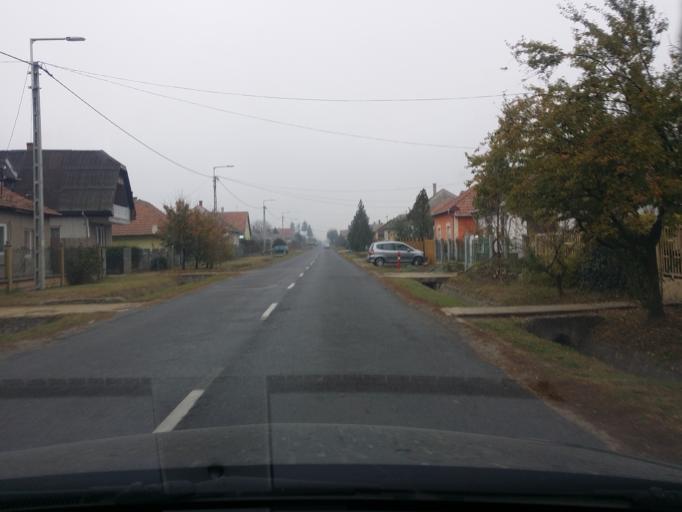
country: HU
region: Szabolcs-Szatmar-Bereg
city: Kek
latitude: 48.0997
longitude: 21.8827
